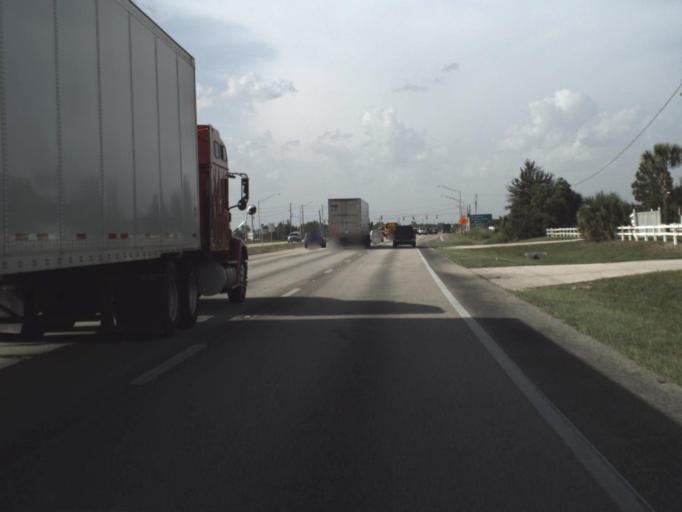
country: US
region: Florida
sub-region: Polk County
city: Dundee
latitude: 27.9755
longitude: -81.6303
